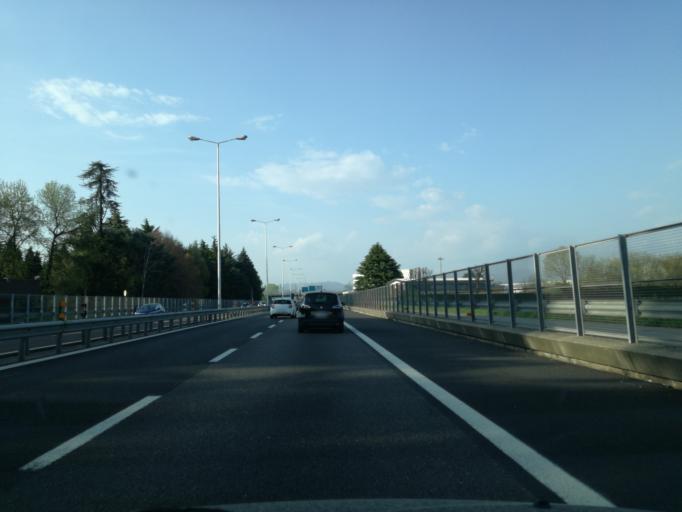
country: IT
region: Lombardy
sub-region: Provincia di Monza e Brianza
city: Velasca
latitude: 45.6291
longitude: 9.3623
